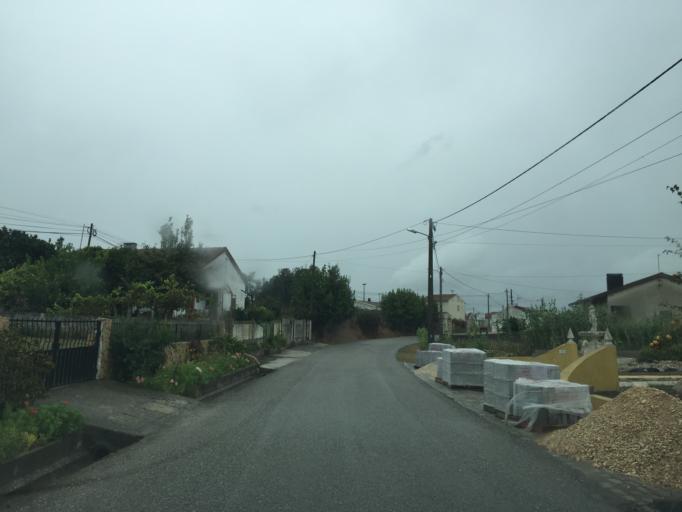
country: PT
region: Coimbra
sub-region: Figueira da Foz
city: Lavos
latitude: 40.0611
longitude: -8.8107
